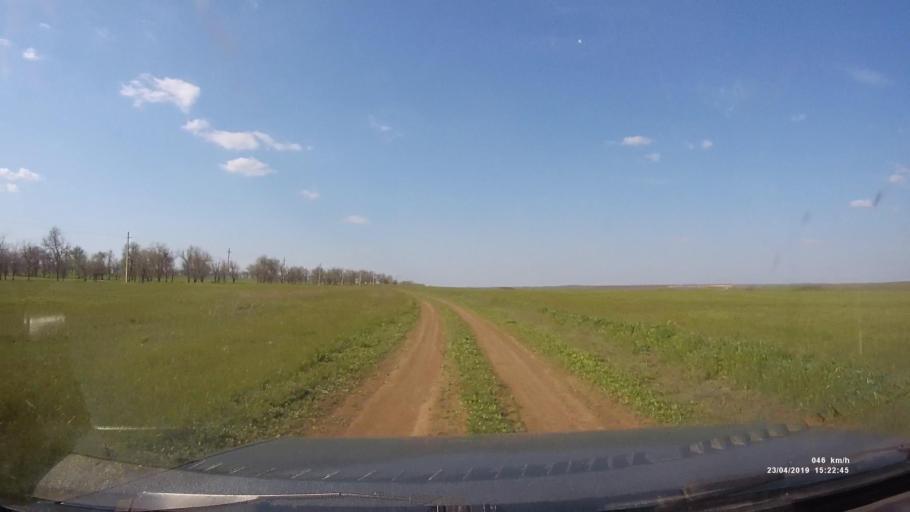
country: RU
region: Rostov
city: Remontnoye
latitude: 46.5311
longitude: 42.9705
